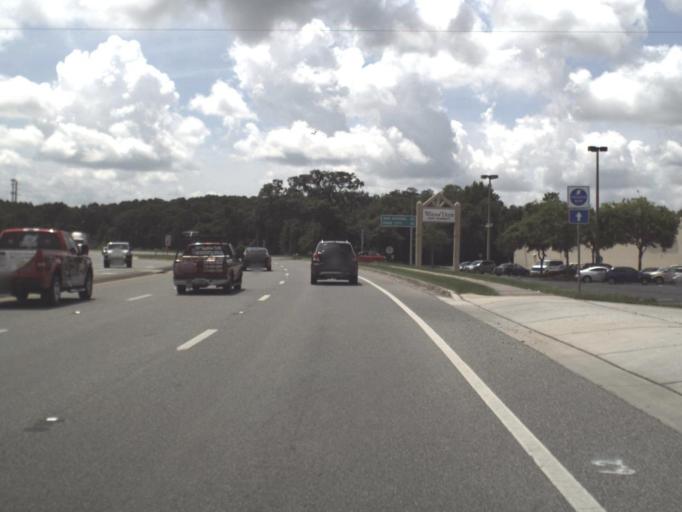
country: US
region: Florida
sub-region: Pasco County
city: Bayonet Point
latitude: 28.3342
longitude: -82.6021
